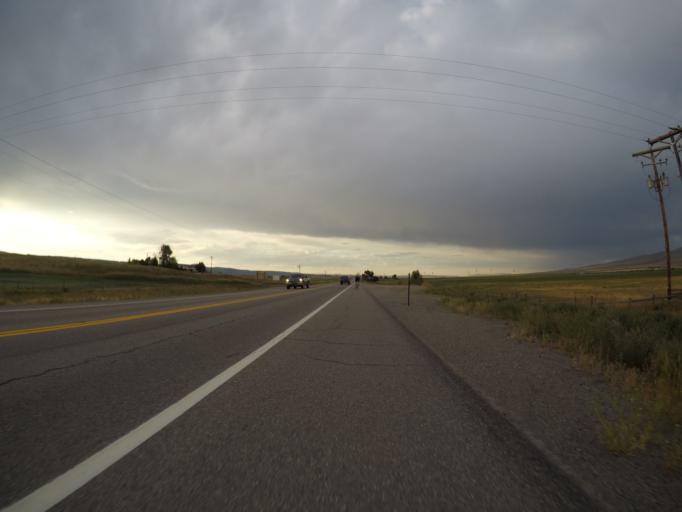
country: US
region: Idaho
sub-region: Bear Lake County
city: Montpelier
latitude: 42.0783
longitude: -110.9466
